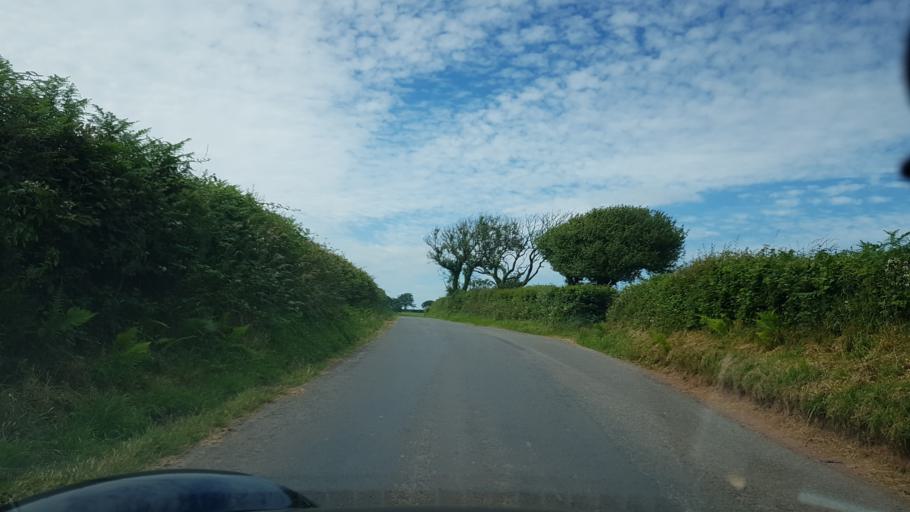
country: GB
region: Wales
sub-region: Carmarthenshire
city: Llanddowror
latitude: 51.7682
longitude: -4.5273
